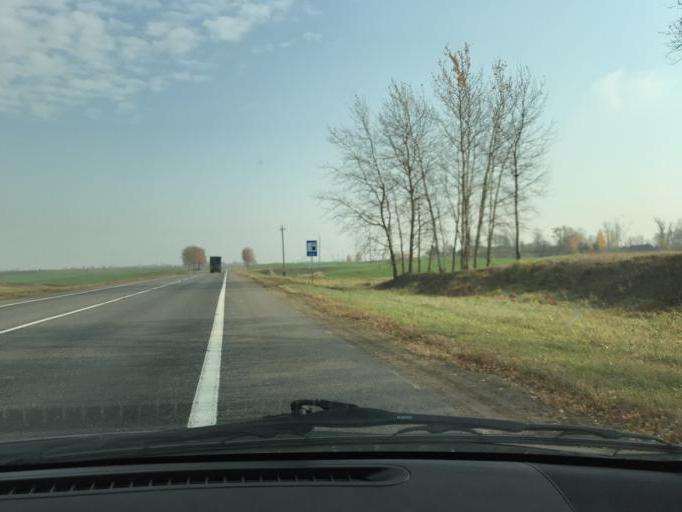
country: BY
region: Vitebsk
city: Chashniki
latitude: 55.0134
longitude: 29.1028
